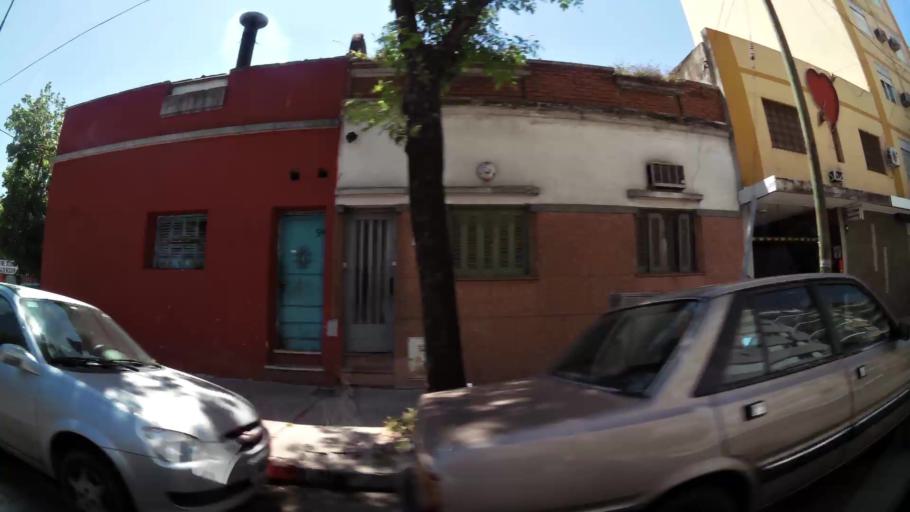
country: AR
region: Buenos Aires
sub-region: Partido de Avellaneda
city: Avellaneda
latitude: -34.6474
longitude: -58.4152
